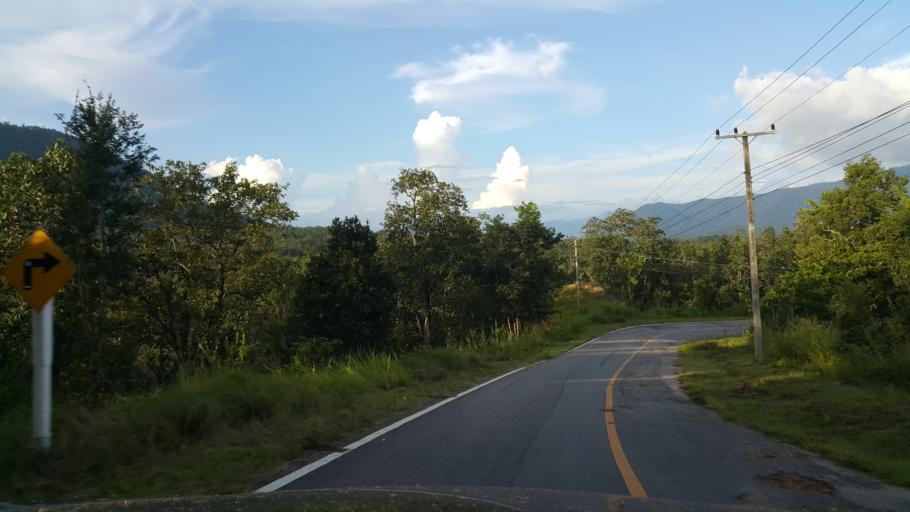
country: TH
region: Mae Hong Son
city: Mae Hi
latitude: 19.1785
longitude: 98.3975
